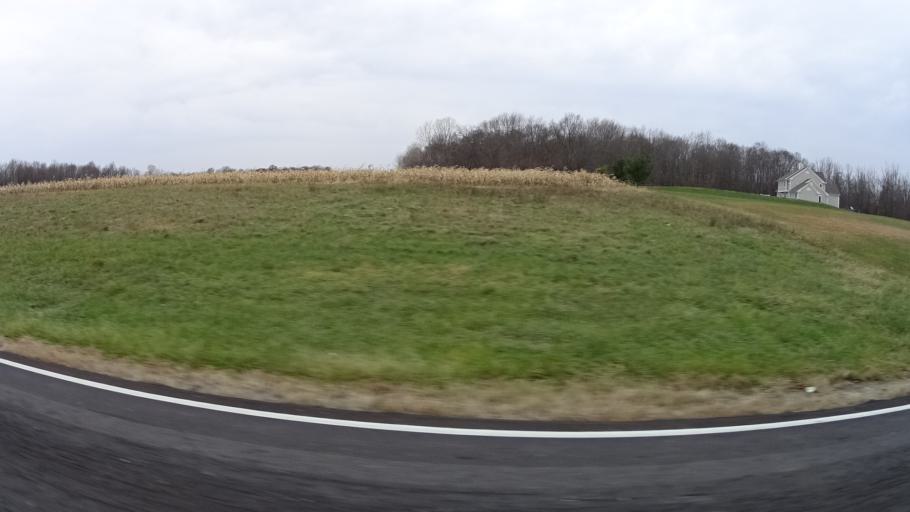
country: US
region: Ohio
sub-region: Lorain County
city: Lagrange
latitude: 41.1848
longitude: -82.0821
